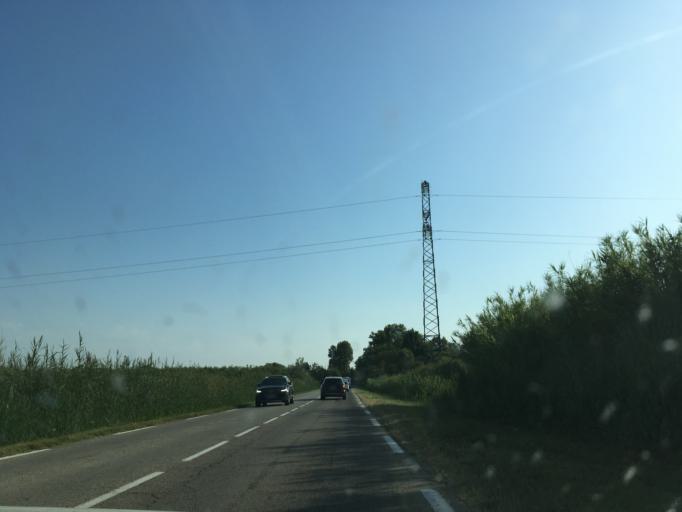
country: FR
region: Languedoc-Roussillon
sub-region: Departement du Gard
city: Fourques
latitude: 43.6483
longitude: 4.5734
